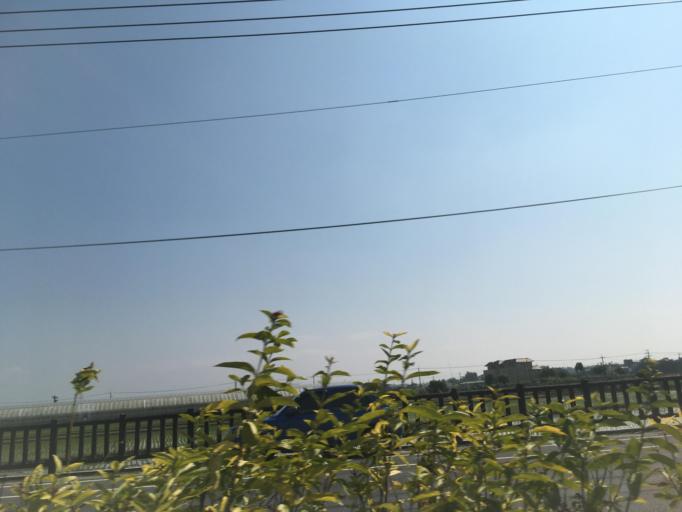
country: TW
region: Taiwan
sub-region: Chiayi
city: Jiayi Shi
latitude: 23.5563
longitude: 120.4376
